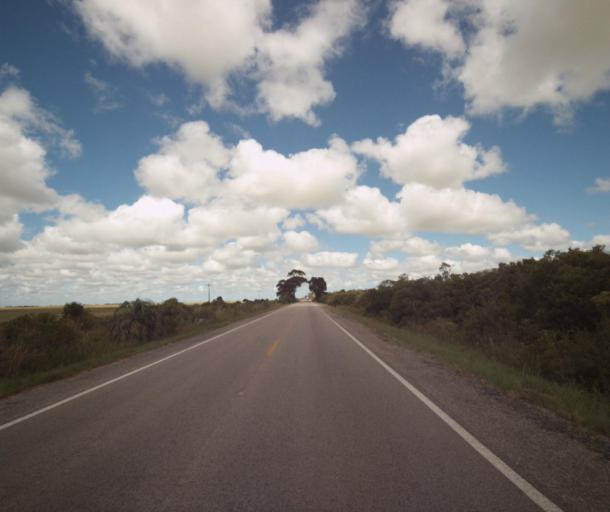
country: BR
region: Rio Grande do Sul
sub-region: Rio Grande
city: Rio Grande
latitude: -32.1867
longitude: -52.4295
